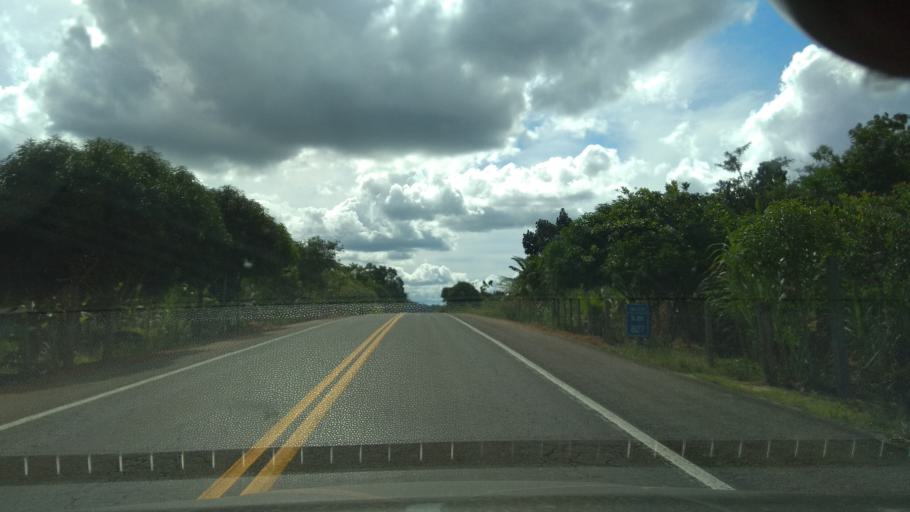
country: BR
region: Bahia
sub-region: Ubaitaba
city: Ubaitaba
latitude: -14.2571
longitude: -39.3531
